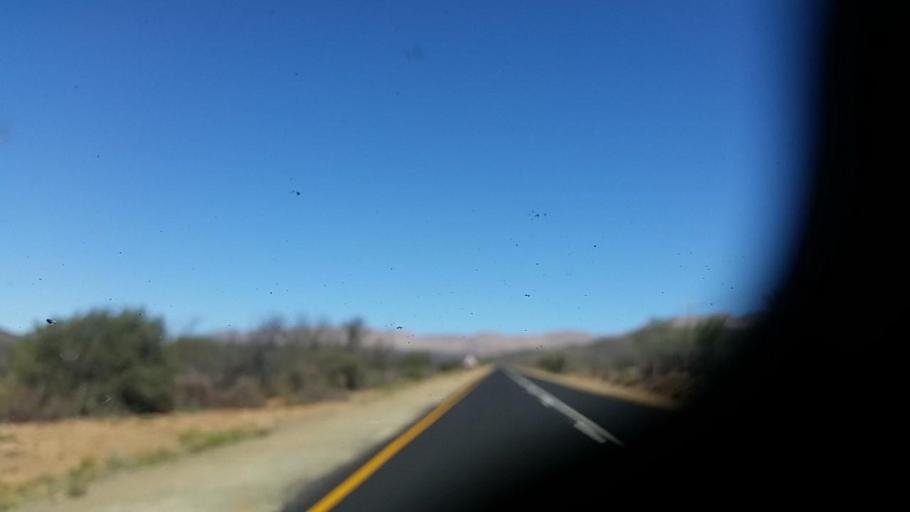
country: ZA
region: Western Cape
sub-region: Eden District Municipality
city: George
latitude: -33.5366
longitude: 22.7193
